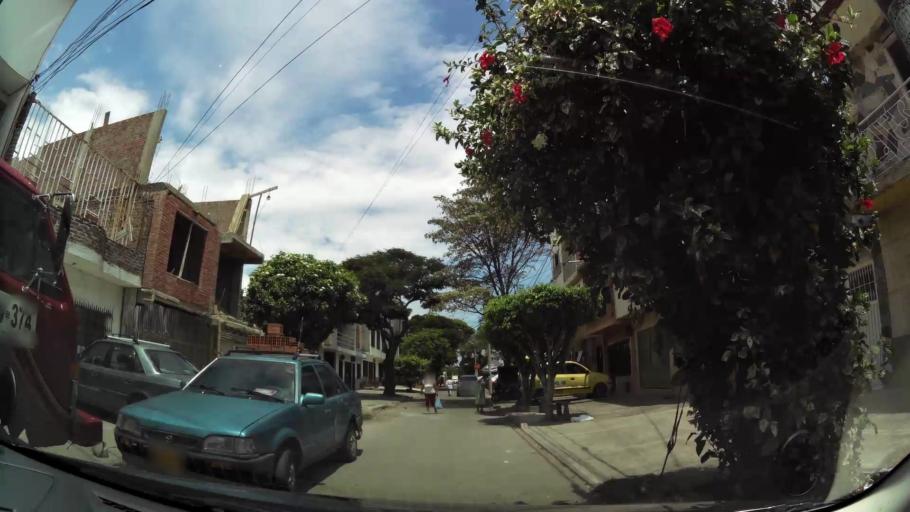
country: CO
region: Valle del Cauca
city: Cali
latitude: 3.4430
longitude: -76.4975
